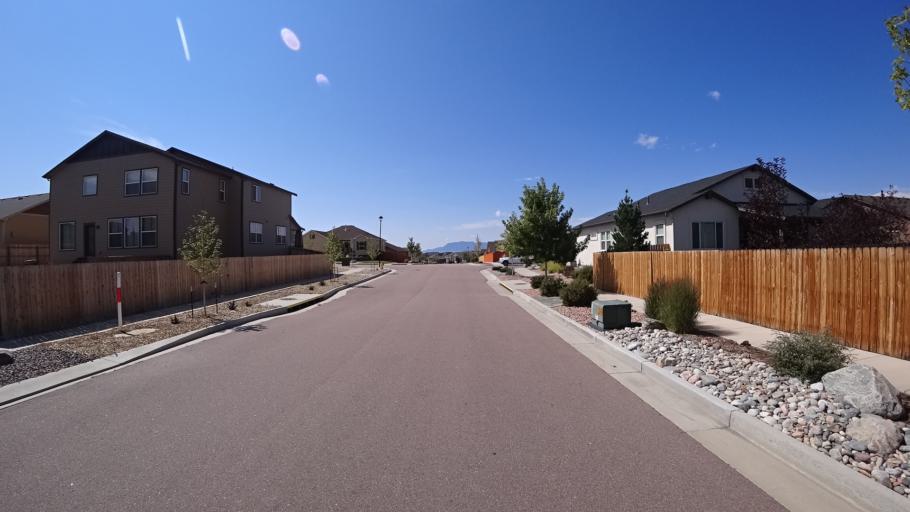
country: US
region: Colorado
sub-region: El Paso County
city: Cimarron Hills
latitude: 38.9320
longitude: -104.6841
